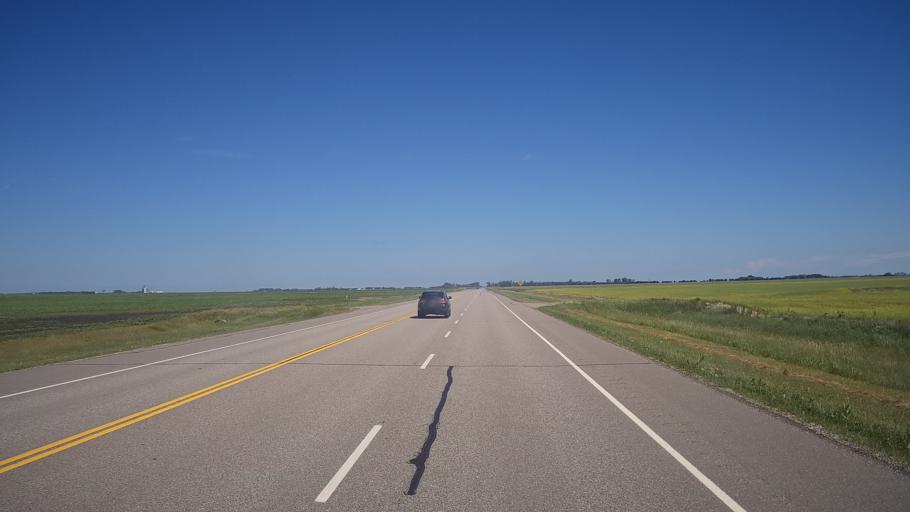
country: CA
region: Manitoba
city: Portage la Prairie
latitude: 50.0294
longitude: -98.4692
